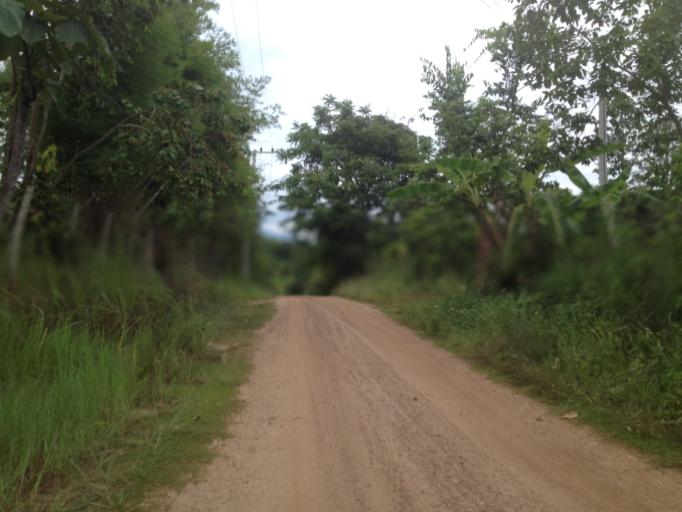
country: TH
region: Chiang Mai
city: Hang Dong
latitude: 18.7118
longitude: 98.8729
